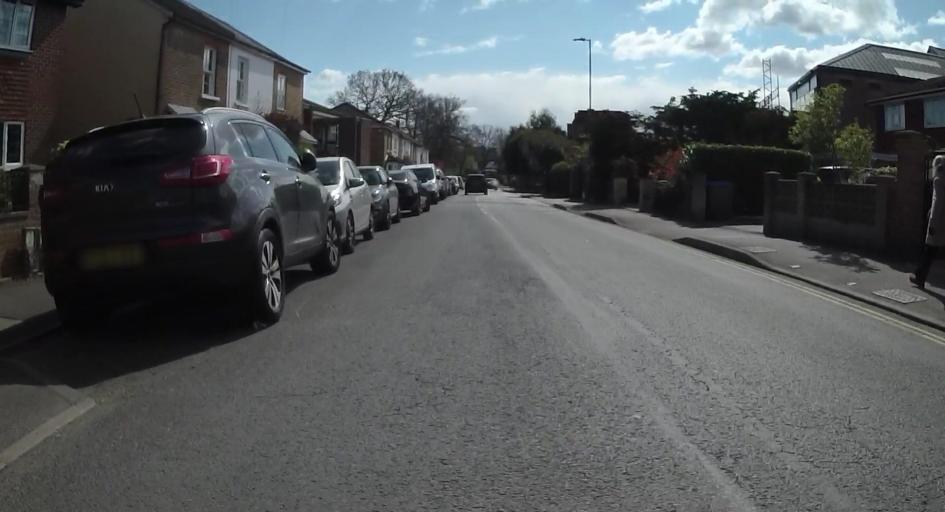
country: GB
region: England
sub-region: Surrey
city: Weybridge
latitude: 51.3768
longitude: -0.4546
